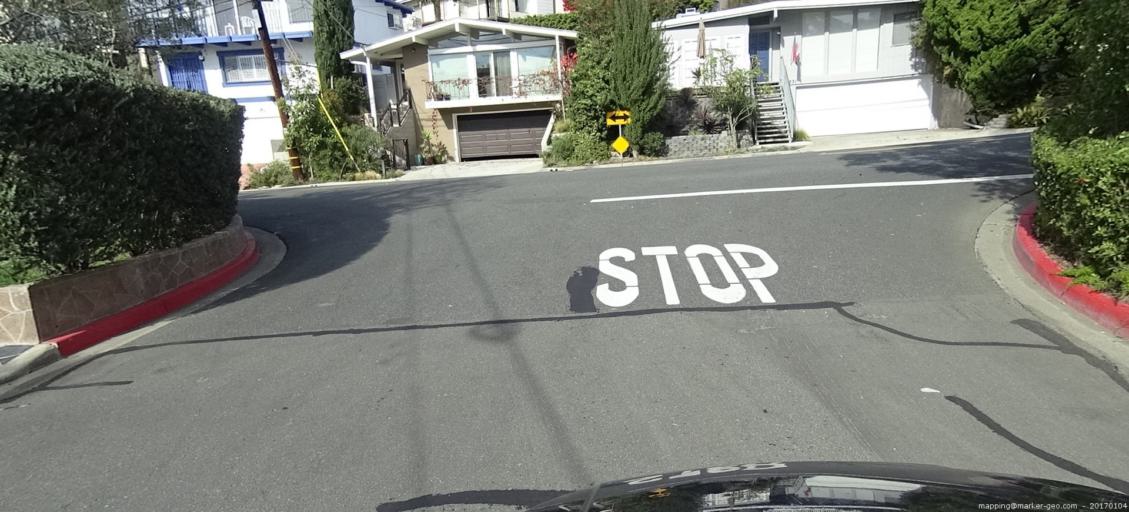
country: US
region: California
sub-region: Orange County
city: Dana Point
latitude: 33.4689
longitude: -117.6896
